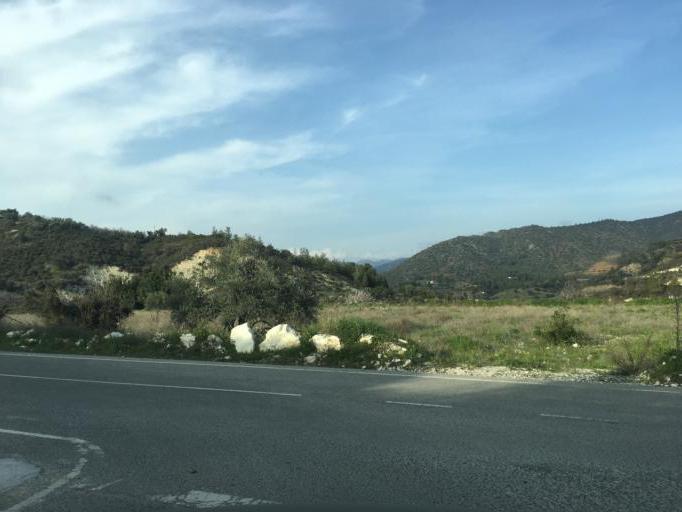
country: CY
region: Limassol
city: Pelendri
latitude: 34.8118
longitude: 32.9600
